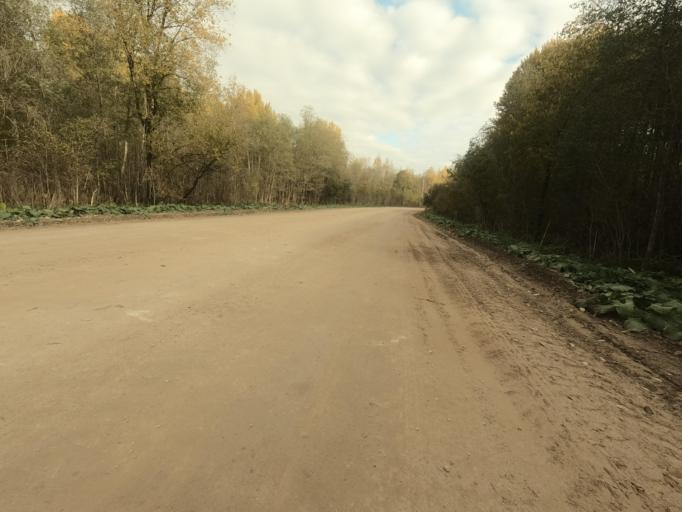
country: RU
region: Novgorod
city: Batetskiy
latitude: 58.8016
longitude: 30.6434
